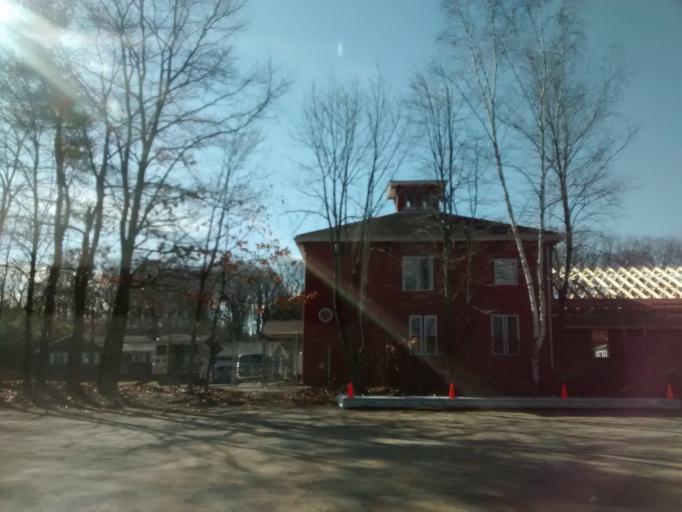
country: US
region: Massachusetts
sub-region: Worcester County
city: Whitinsville
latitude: 42.1080
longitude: -71.6671
